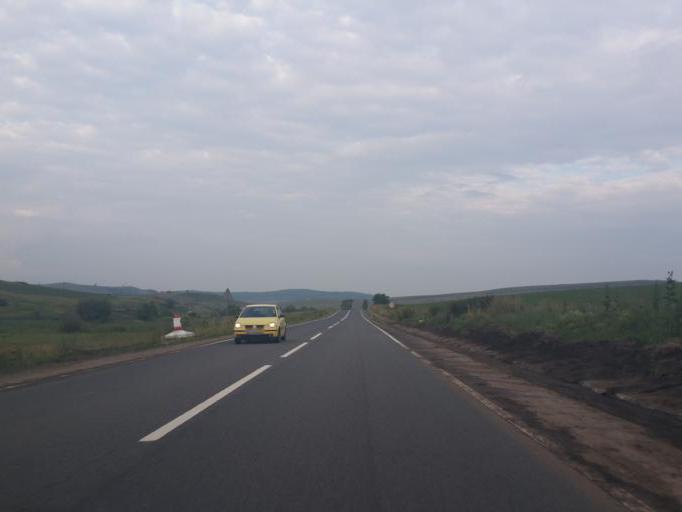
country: RO
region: Cluj
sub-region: Comuna Sanpaul
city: Sanpaul
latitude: 46.9215
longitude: 23.4124
